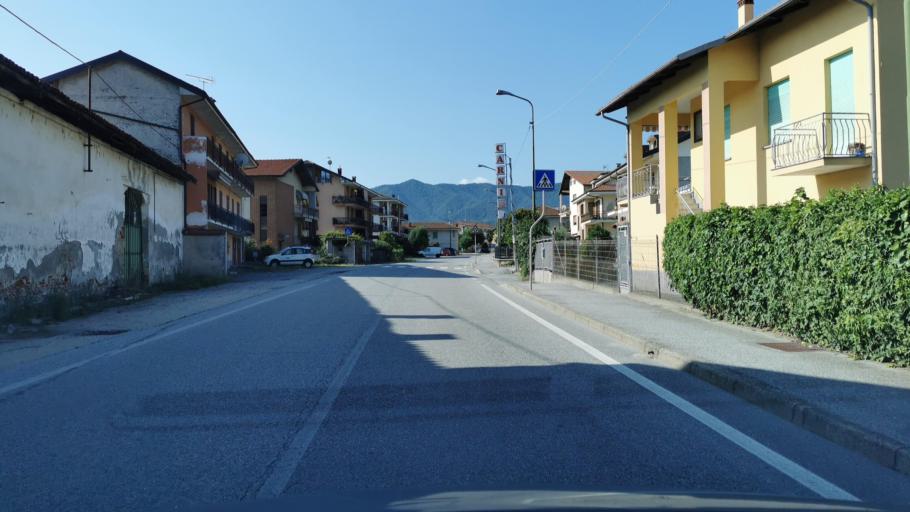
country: IT
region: Piedmont
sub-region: Provincia di Cuneo
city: Revello
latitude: 44.6586
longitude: 7.3933
